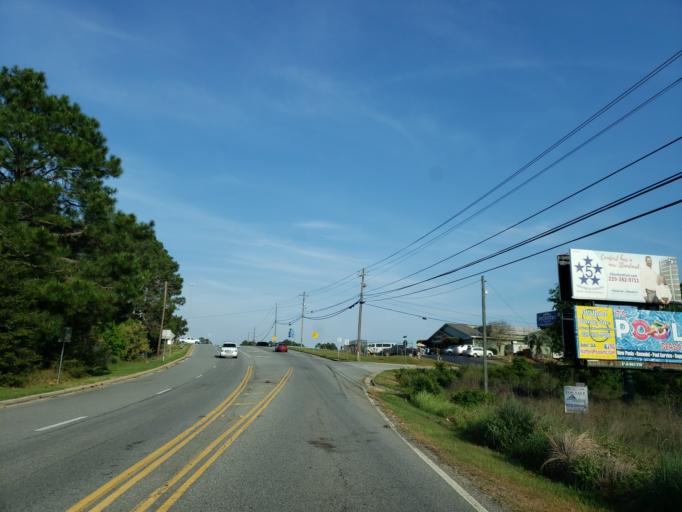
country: US
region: Georgia
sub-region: Tift County
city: Tifton
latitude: 31.4638
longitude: -83.5321
